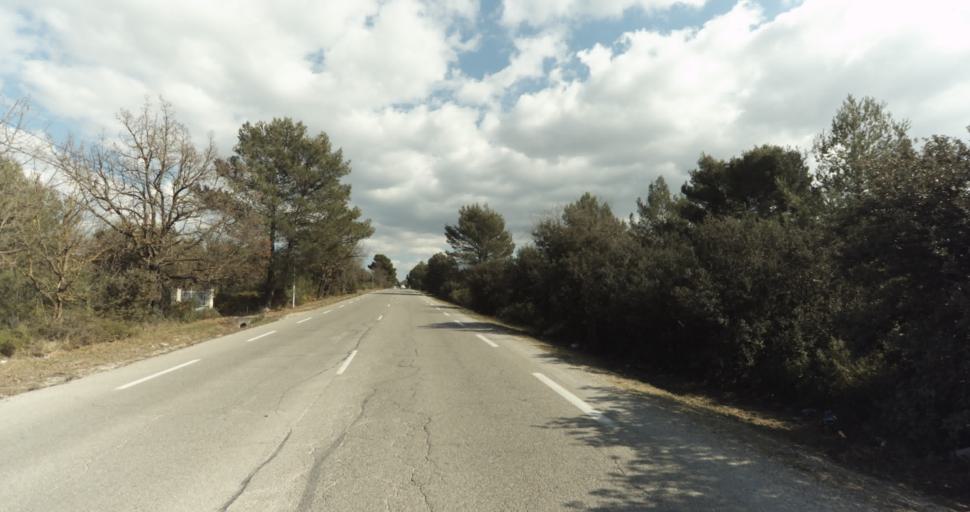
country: FR
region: Provence-Alpes-Cote d'Azur
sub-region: Departement des Bouches-du-Rhone
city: Greasque
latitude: 43.4475
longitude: 5.5132
